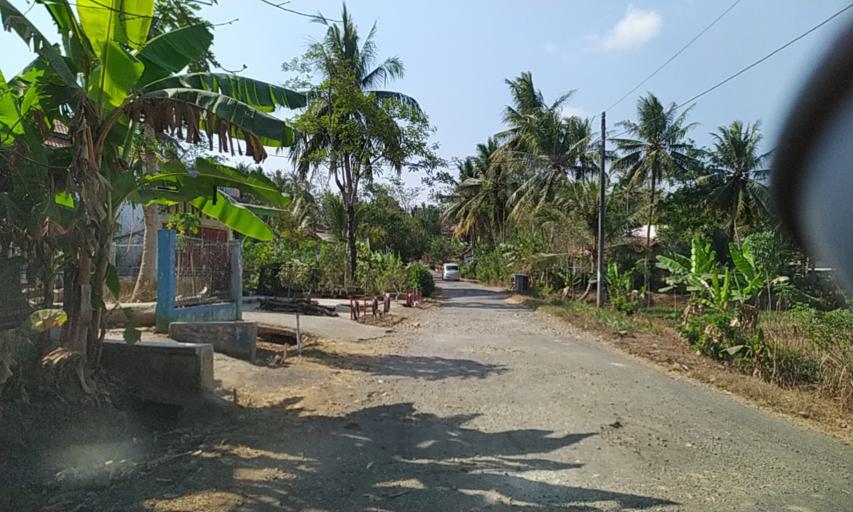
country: ID
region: Central Java
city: Ciloning
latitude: -7.4881
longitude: 108.8586
